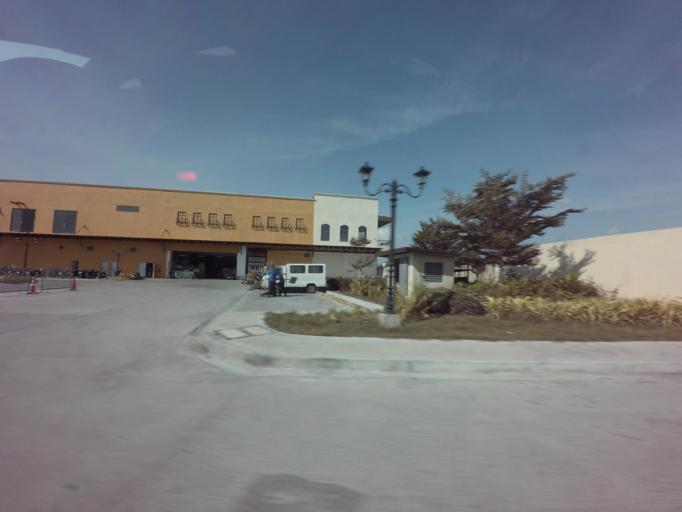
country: PH
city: Sambayanihan People's Village
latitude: 14.4758
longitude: 120.9844
